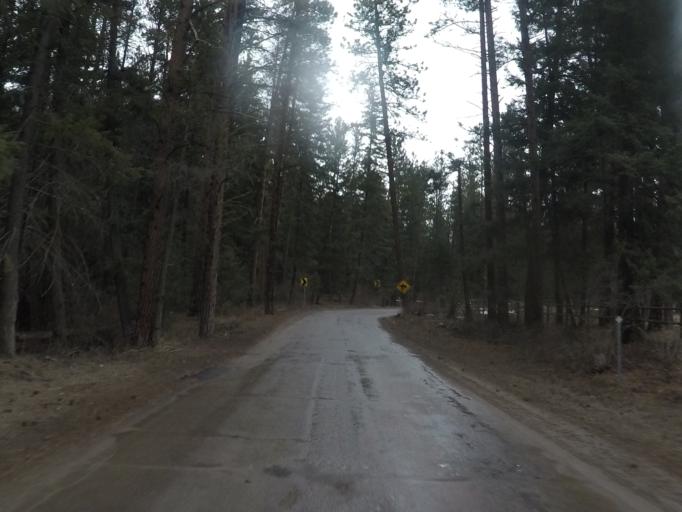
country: US
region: Montana
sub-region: Missoula County
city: East Missoula
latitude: 46.9200
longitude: -113.9598
